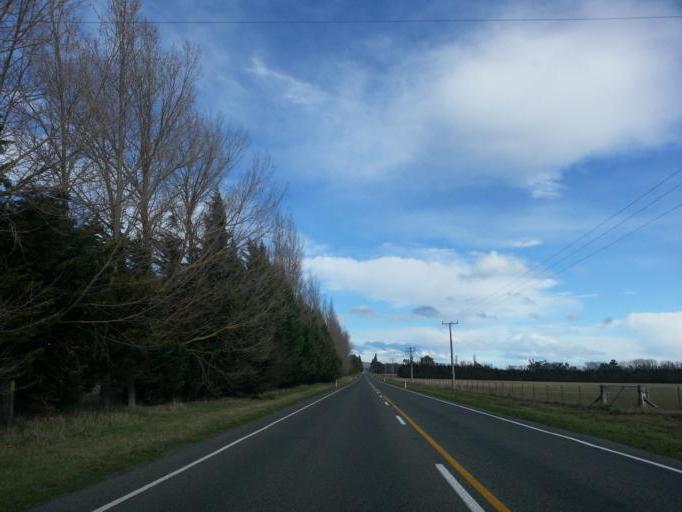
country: NZ
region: Canterbury
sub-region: Hurunui District
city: Amberley
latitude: -42.7823
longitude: 172.8416
